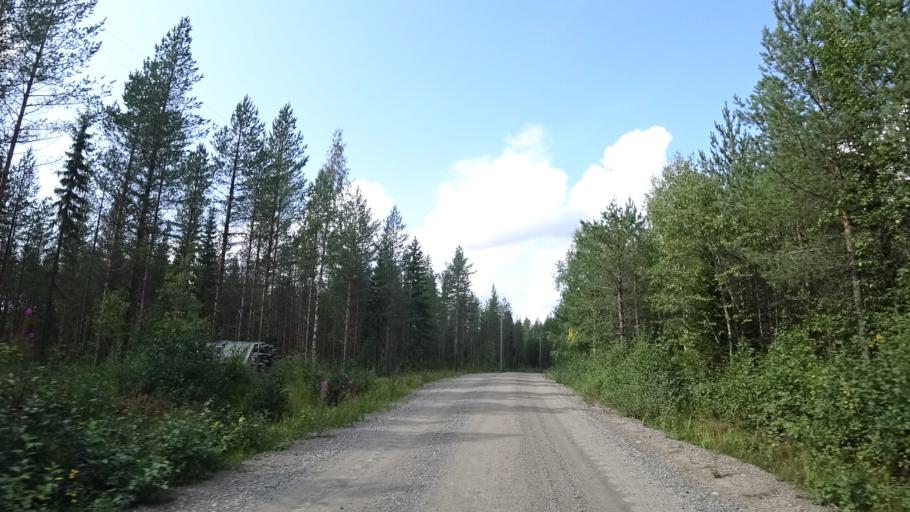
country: FI
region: North Karelia
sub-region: Joensuu
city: Ilomantsi
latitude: 62.9277
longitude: 31.3270
